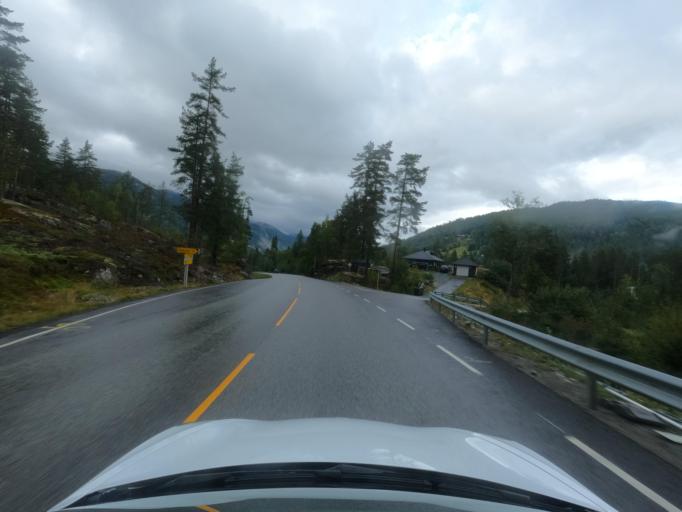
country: NO
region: Telemark
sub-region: Seljord
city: Seljord
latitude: 59.4471
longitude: 8.5621
